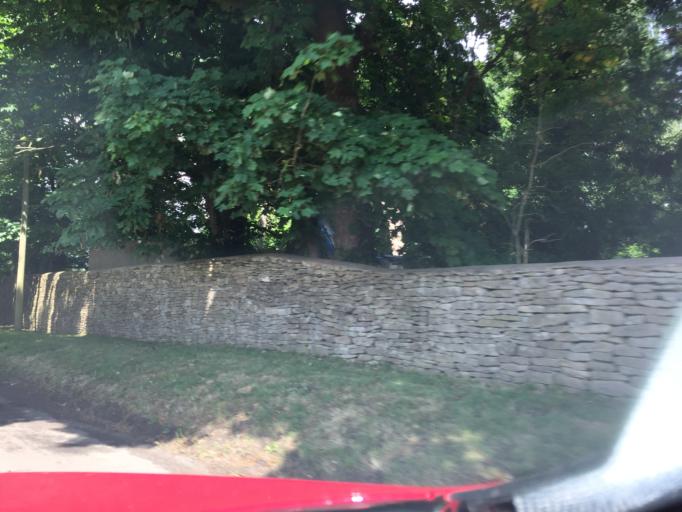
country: GB
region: England
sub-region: Gloucestershire
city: Chalford
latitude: 51.6850
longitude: -2.1429
